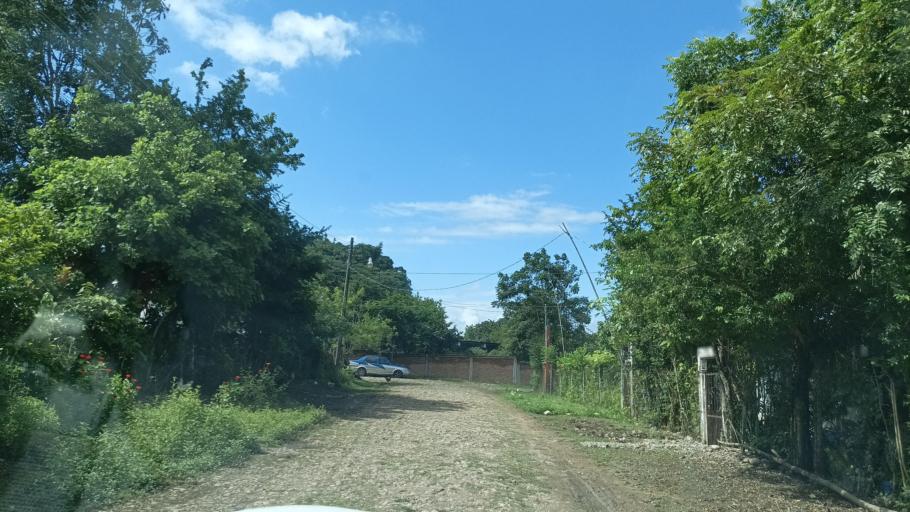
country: MX
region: Veracruz
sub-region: Tantoyuca
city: El Lindero
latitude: 21.1929
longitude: -98.1450
